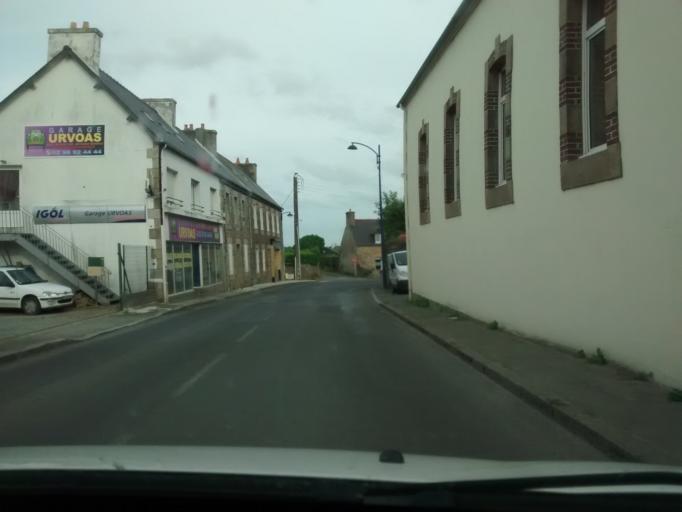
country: FR
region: Brittany
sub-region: Departement des Cotes-d'Armor
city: Plouguiel
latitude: 48.7970
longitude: -3.2375
